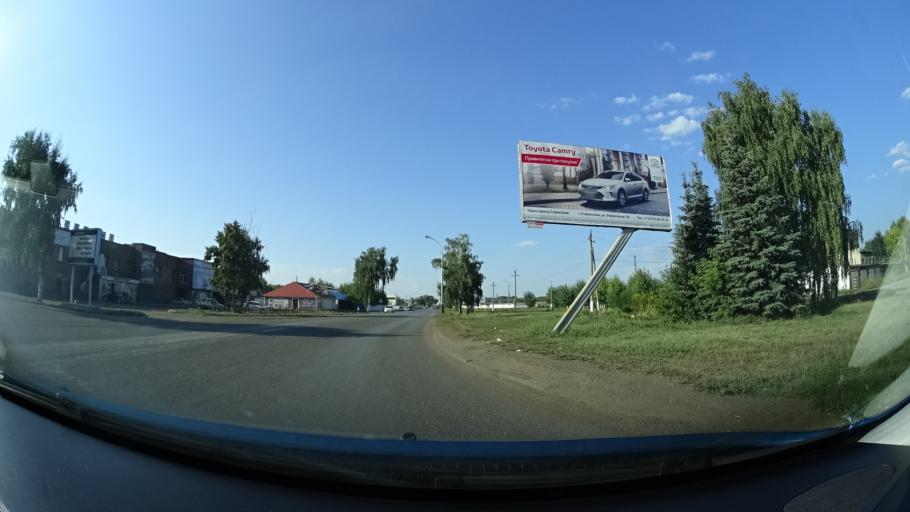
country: RU
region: Bashkortostan
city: Salavat
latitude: 53.3743
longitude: 55.9256
